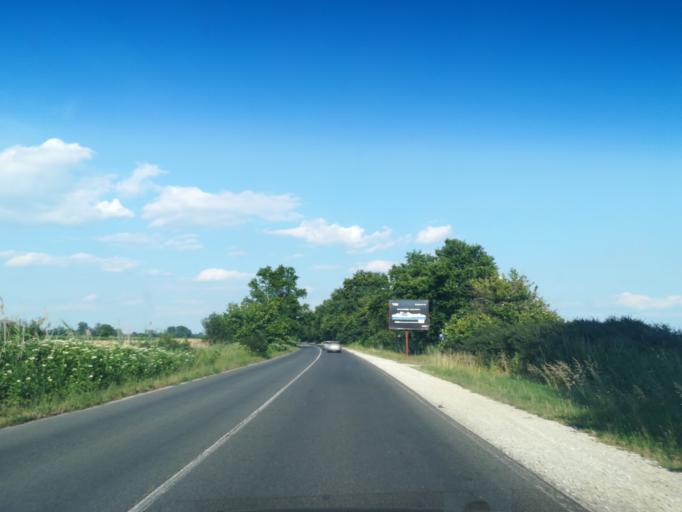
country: BG
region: Plovdiv
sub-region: Obshtina Sadovo
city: Sadovo
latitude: 42.1464
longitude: 24.8467
